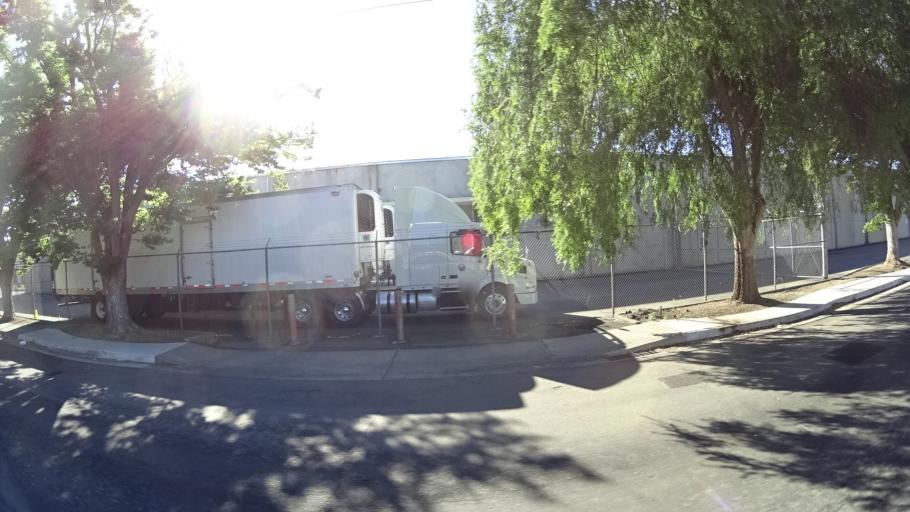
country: US
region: California
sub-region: Sacramento County
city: Sacramento
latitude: 38.5994
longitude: -121.4992
